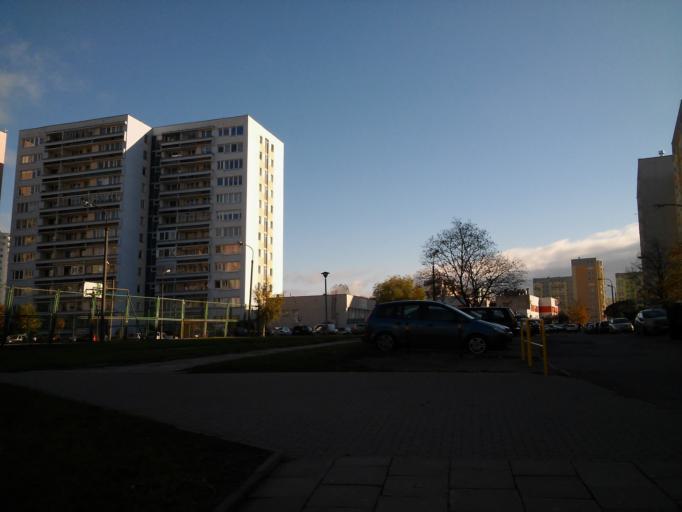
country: PL
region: Pomeranian Voivodeship
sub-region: Powiat gdanski
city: Kowale
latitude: 54.3581
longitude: 18.5756
